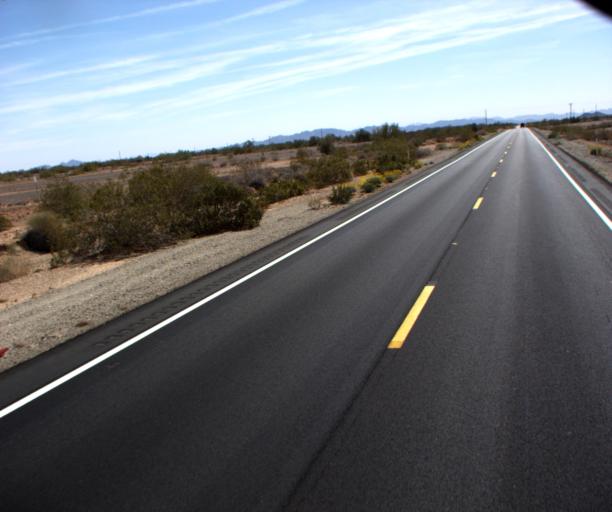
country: US
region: Arizona
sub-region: Yuma County
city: Wellton
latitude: 32.9982
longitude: -114.2863
